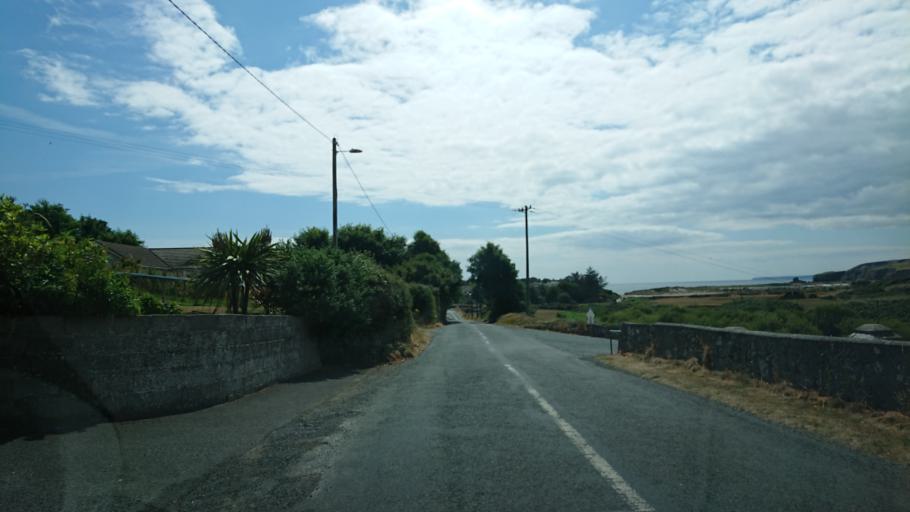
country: IE
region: Munster
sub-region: Waterford
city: Portlaw
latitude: 52.1440
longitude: -7.3566
